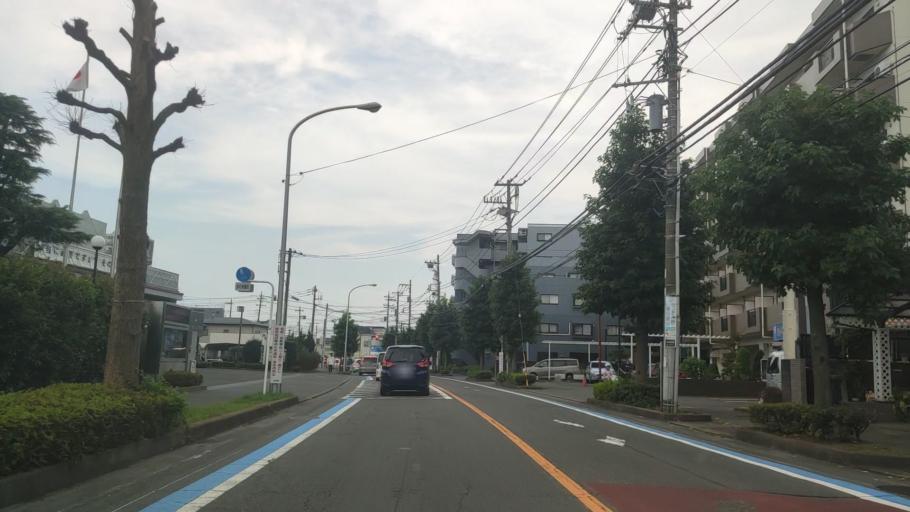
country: JP
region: Kanagawa
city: Minami-rinkan
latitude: 35.5025
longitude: 139.4494
